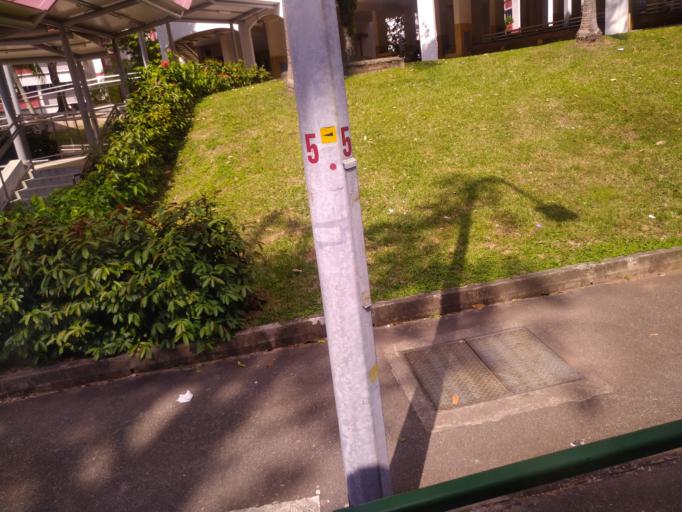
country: SG
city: Singapore
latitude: 1.2873
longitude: 103.8105
